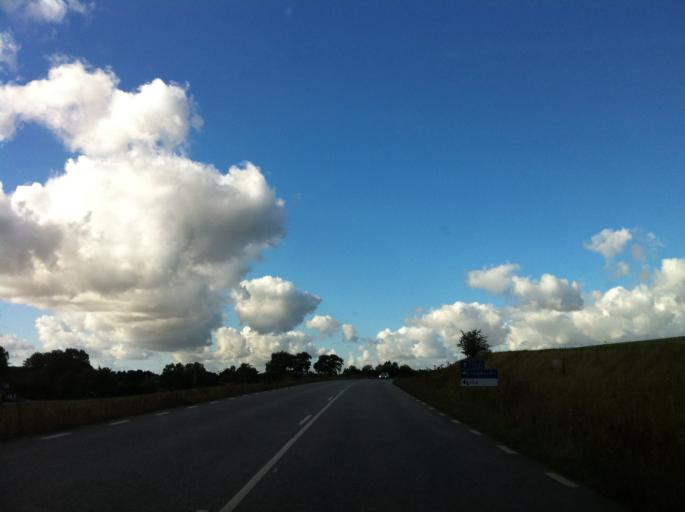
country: SE
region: Skane
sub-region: Eslovs Kommun
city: Eslov
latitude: 55.7618
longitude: 13.3272
